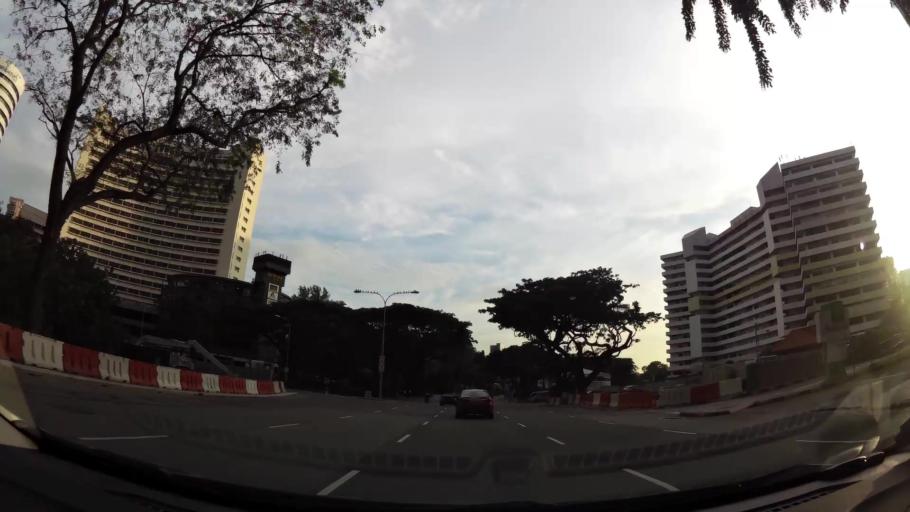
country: SG
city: Singapore
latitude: 1.2886
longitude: 103.8351
